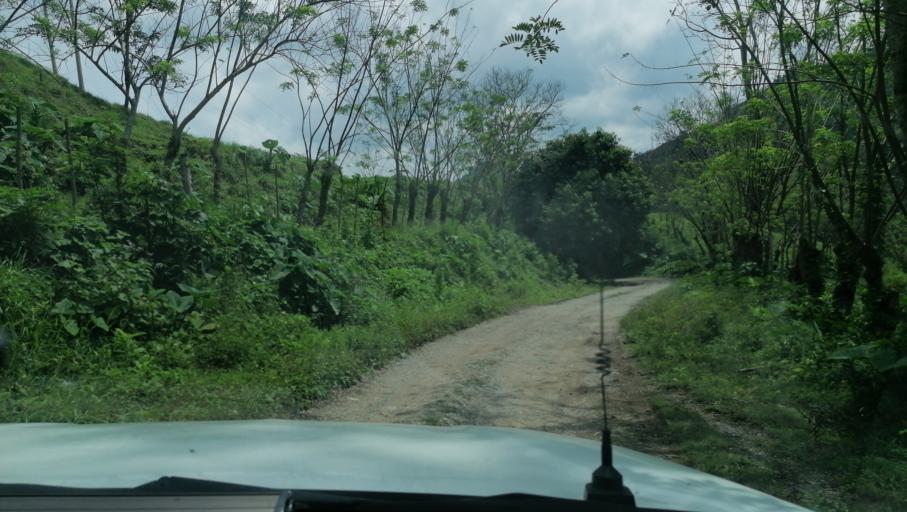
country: MX
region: Chiapas
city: Ixtacomitan
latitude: 17.4446
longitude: -93.2003
